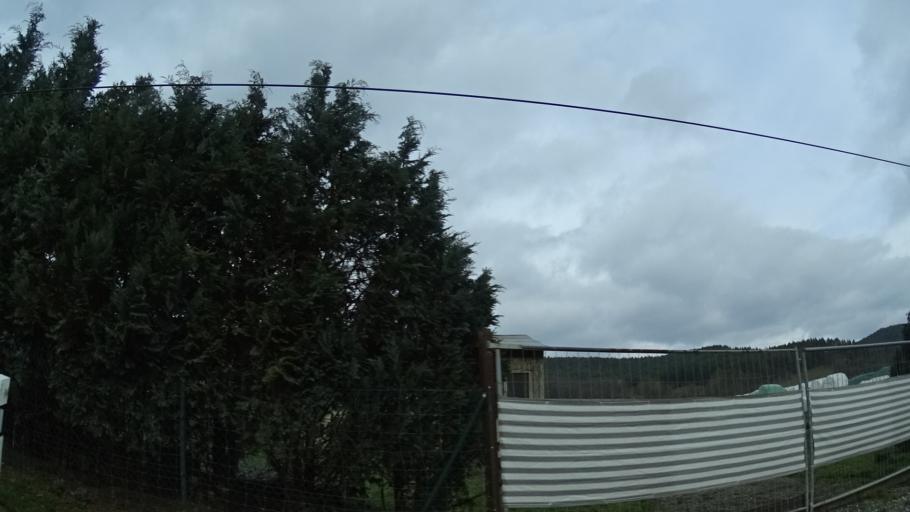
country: DE
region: Thuringia
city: Reinstadt
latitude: 50.7897
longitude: 11.4930
